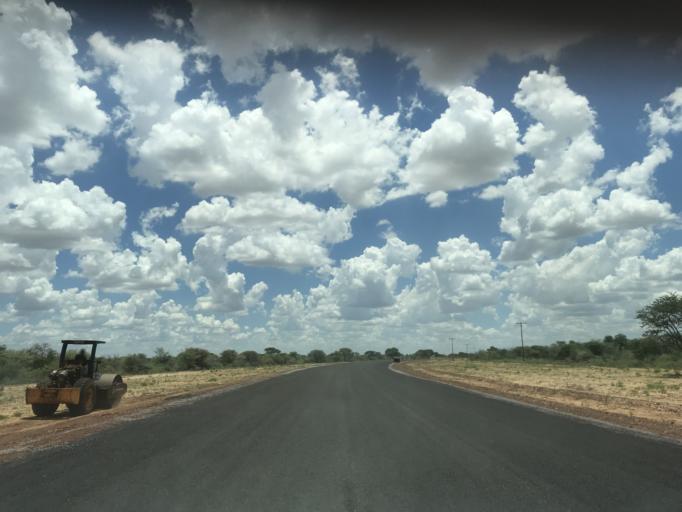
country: BW
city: Mabuli
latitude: -25.8015
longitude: 24.6712
